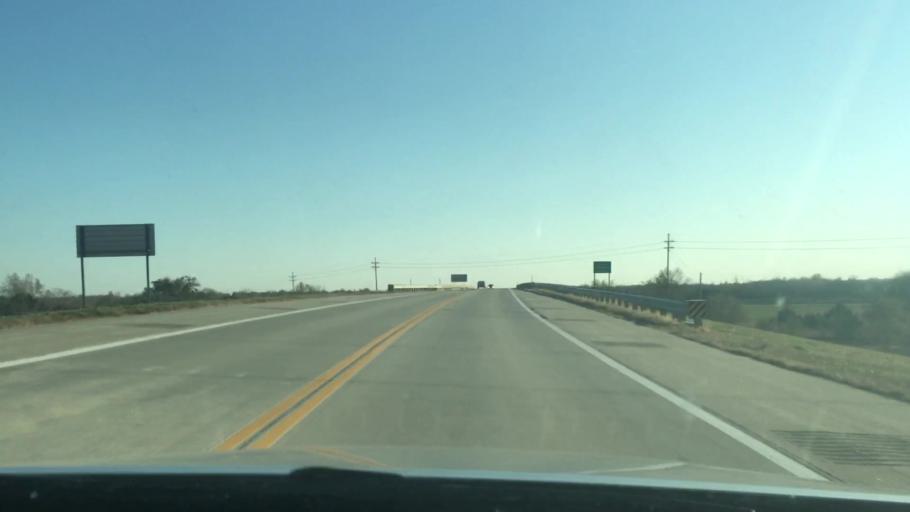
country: US
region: Kansas
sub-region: Reno County
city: Hutchinson
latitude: 38.0844
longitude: -97.9899
